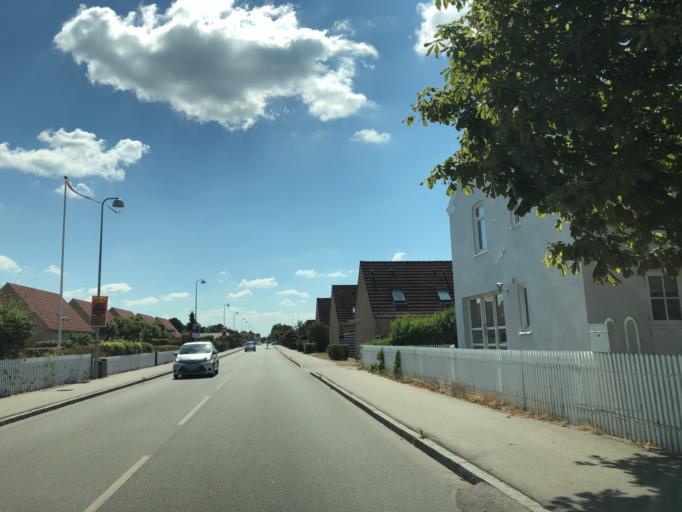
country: DK
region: Capital Region
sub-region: Halsnaes Kommune
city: Hundested
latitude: 55.9553
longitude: 11.8546
